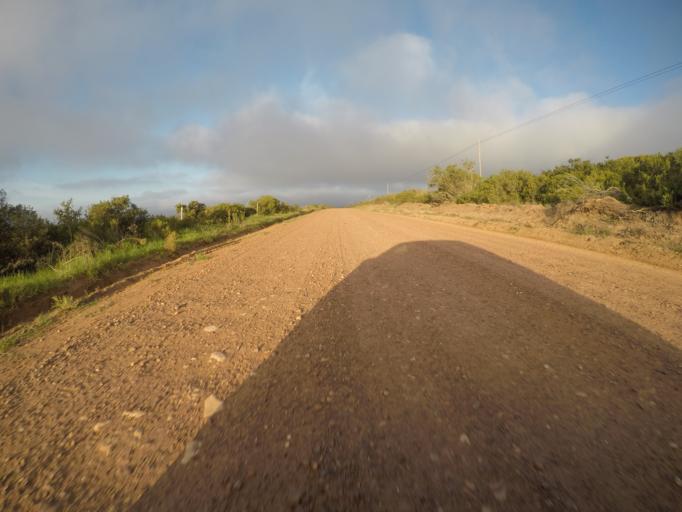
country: ZA
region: Western Cape
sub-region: Eden District Municipality
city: Mossel Bay
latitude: -34.1429
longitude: 22.0282
